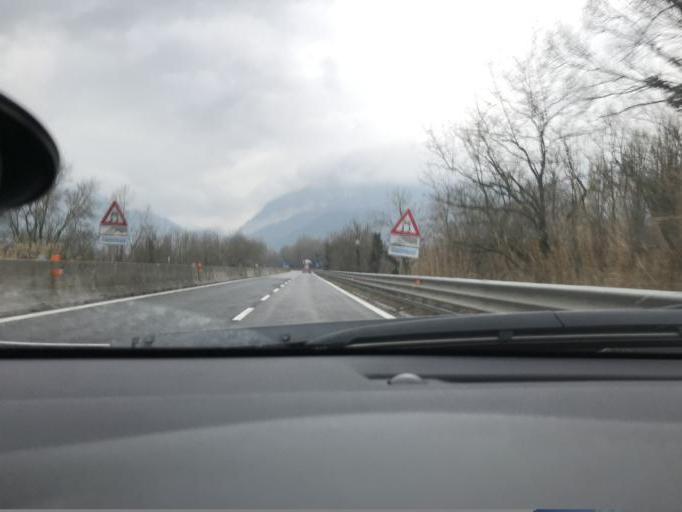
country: IT
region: The Marches
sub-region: Provincia di Ancona
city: Serra San Quirico
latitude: 43.4511
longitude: 13.0409
